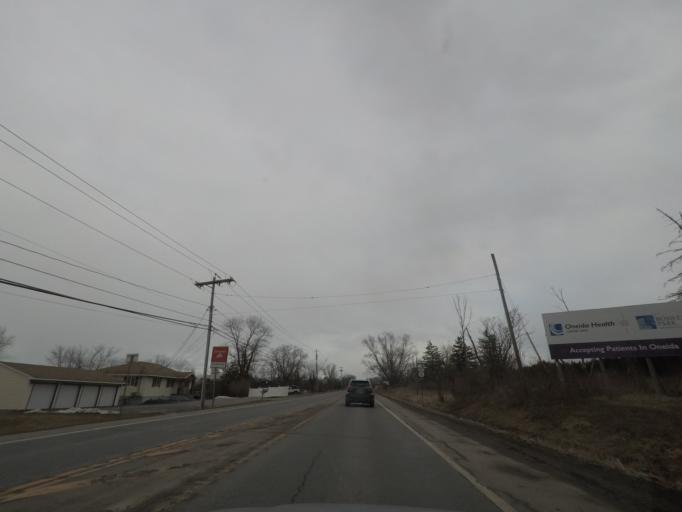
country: US
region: New York
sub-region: Madison County
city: Wampsville
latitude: 43.0763
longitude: -75.6888
